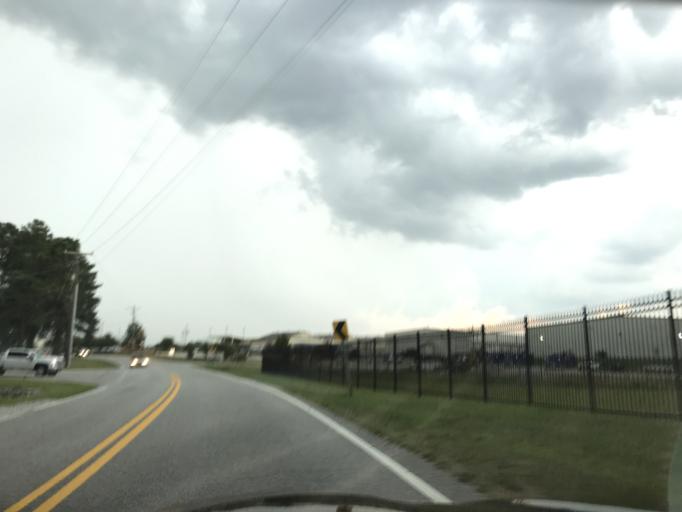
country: US
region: North Carolina
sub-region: Johnston County
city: Wilsons Mills
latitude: 35.5458
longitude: -78.3921
